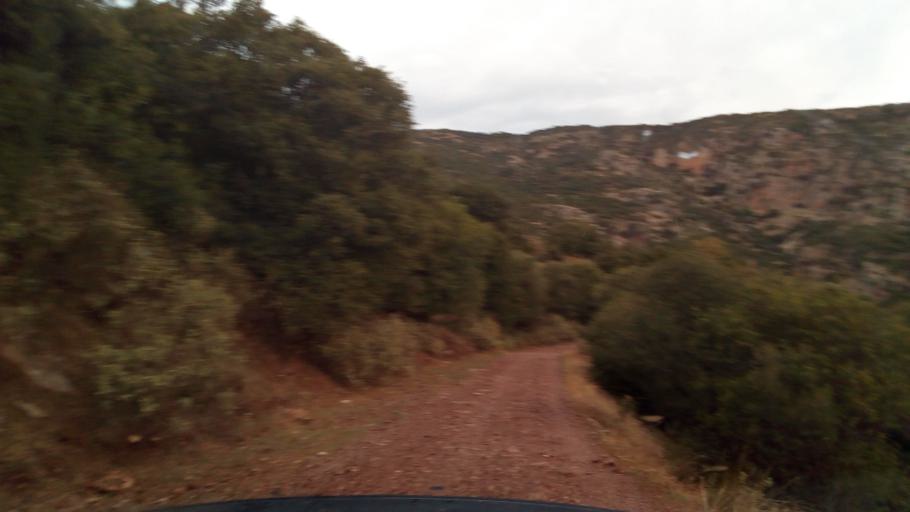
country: GR
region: West Greece
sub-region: Nomos Achaias
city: Kamarai
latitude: 38.4136
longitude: 22.0546
